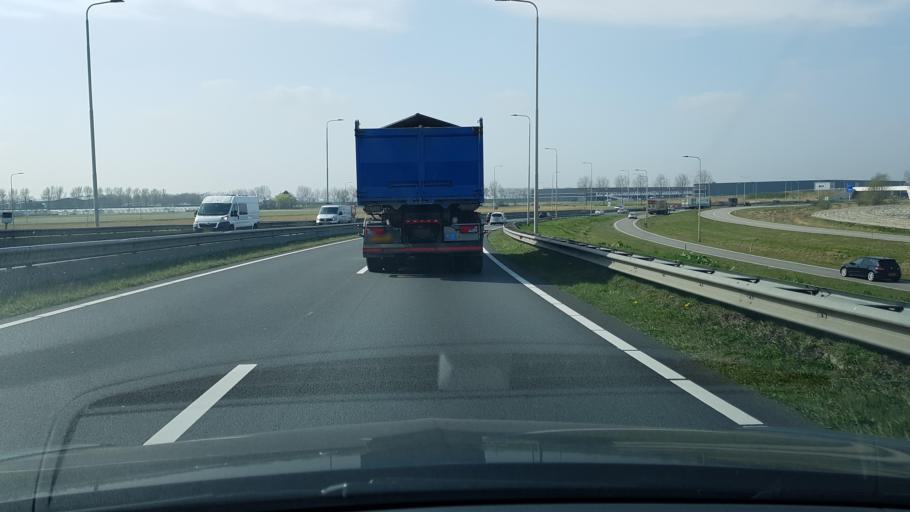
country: NL
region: North Holland
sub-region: Gemeente Aalsmeer
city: Aalsmeer
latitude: 52.2765
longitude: 4.7360
